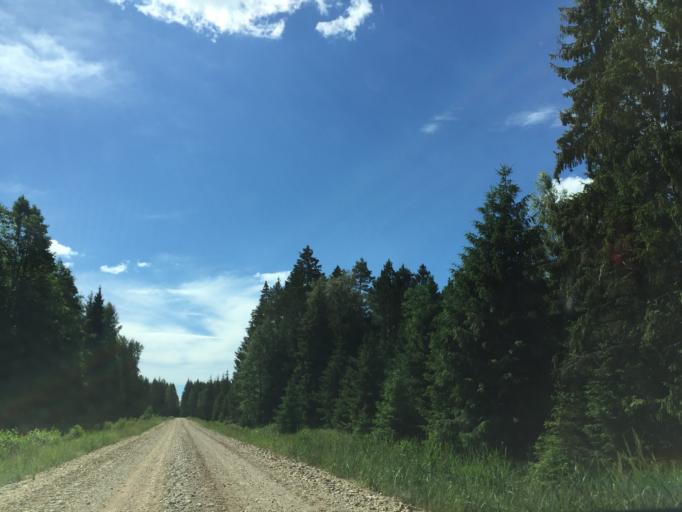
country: LV
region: Ventspils Rajons
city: Piltene
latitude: 57.2541
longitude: 21.8393
